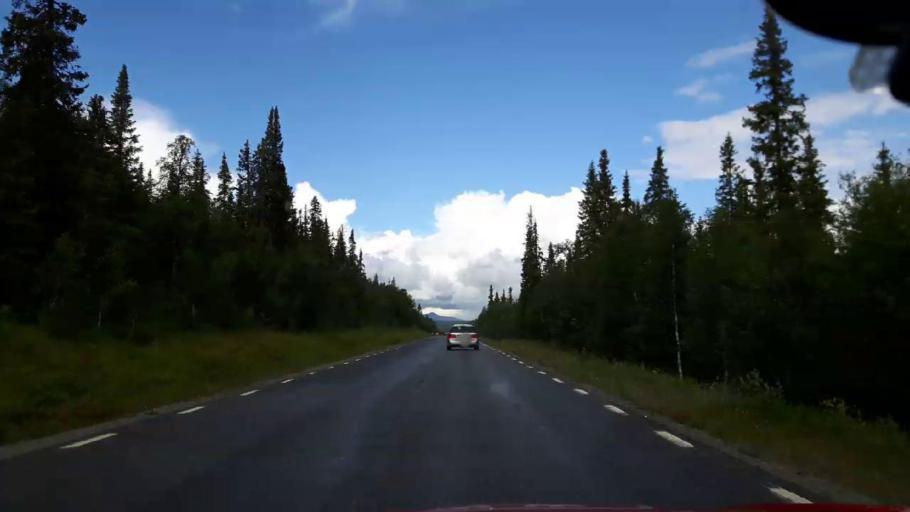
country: SE
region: Vaesterbotten
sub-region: Vilhelmina Kommun
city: Sjoberg
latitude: 65.0270
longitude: 15.1472
